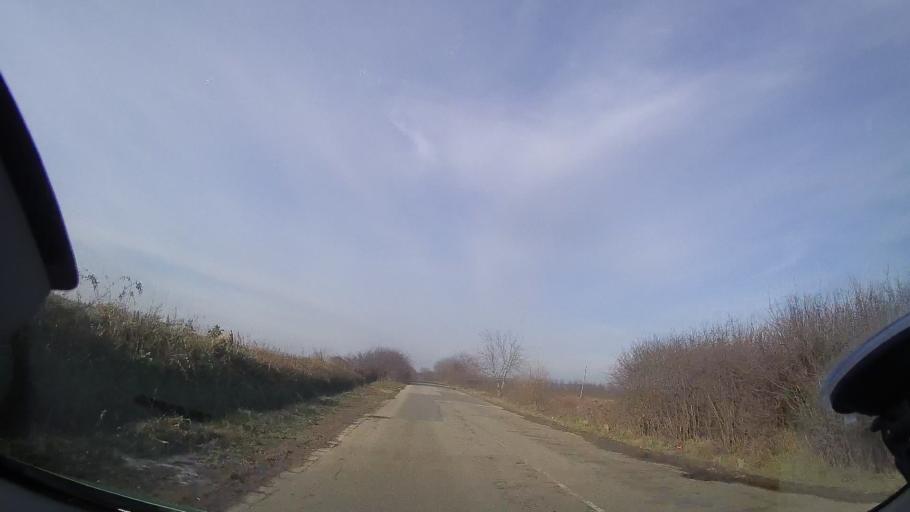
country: RO
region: Bihor
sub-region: Comuna Spinus
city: Spinus
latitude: 47.2095
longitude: 22.1797
